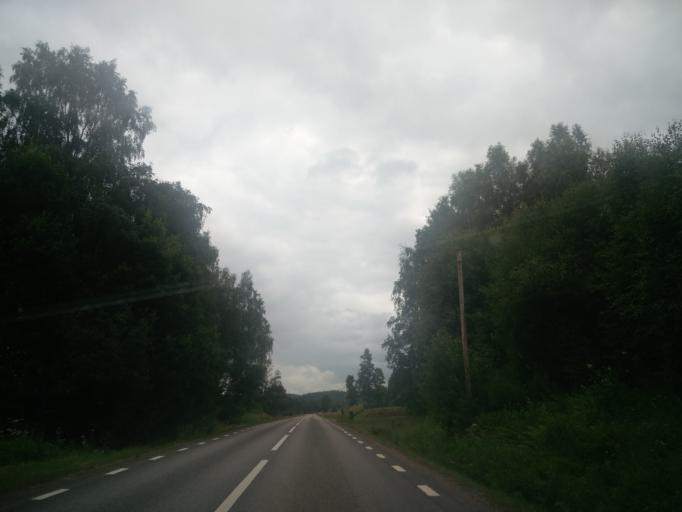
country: SE
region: Vaermland
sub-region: Torsby Kommun
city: Torsby
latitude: 59.9341
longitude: 12.9000
